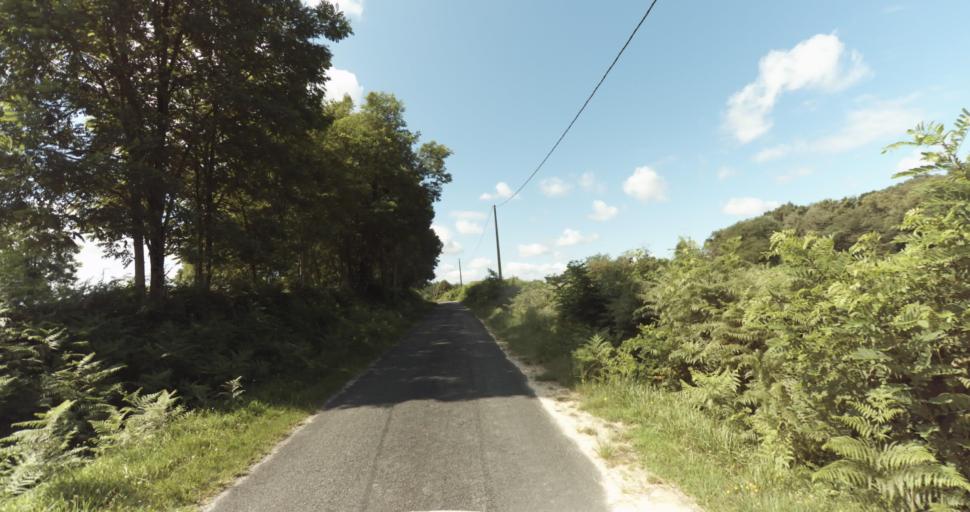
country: FR
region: Aquitaine
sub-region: Departement de la Gironde
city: Bazas
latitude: 44.4680
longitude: -0.2166
